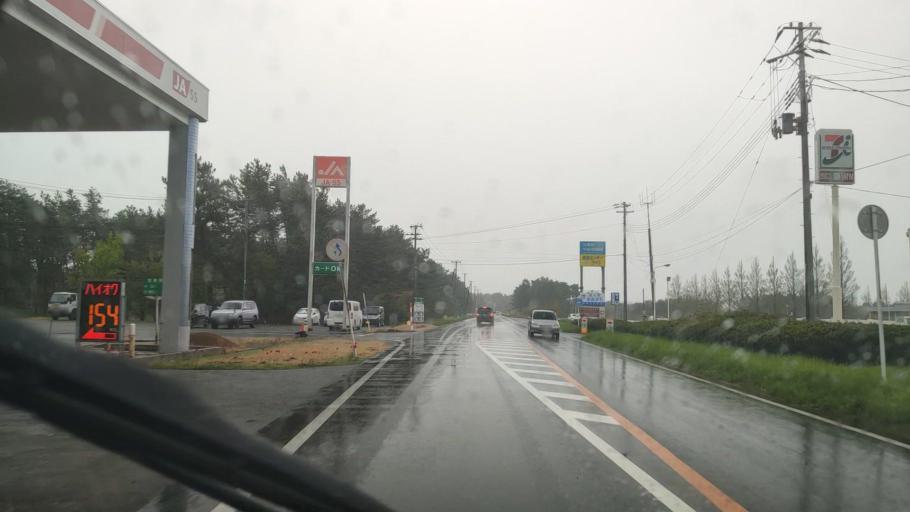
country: JP
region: Akita
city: Tenno
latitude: 40.0167
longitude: 139.9528
